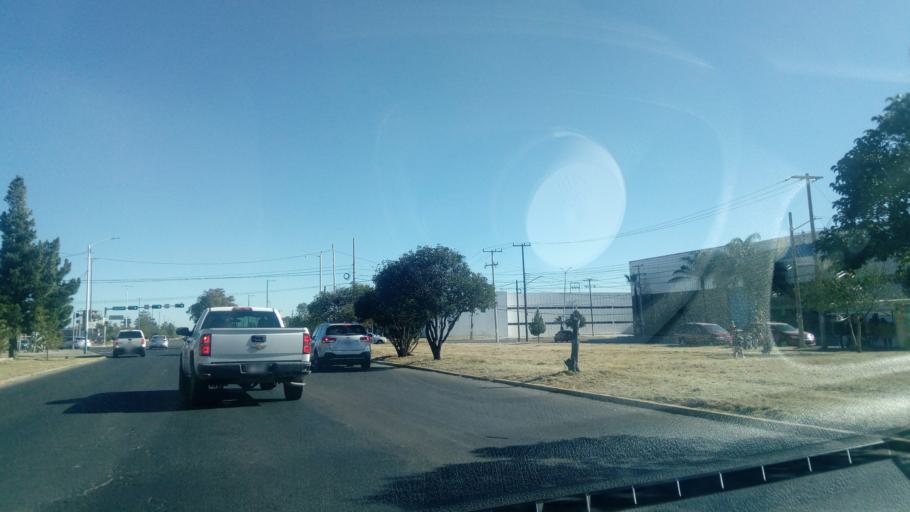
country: MX
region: Durango
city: Victoria de Durango
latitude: 24.0666
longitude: -104.6017
